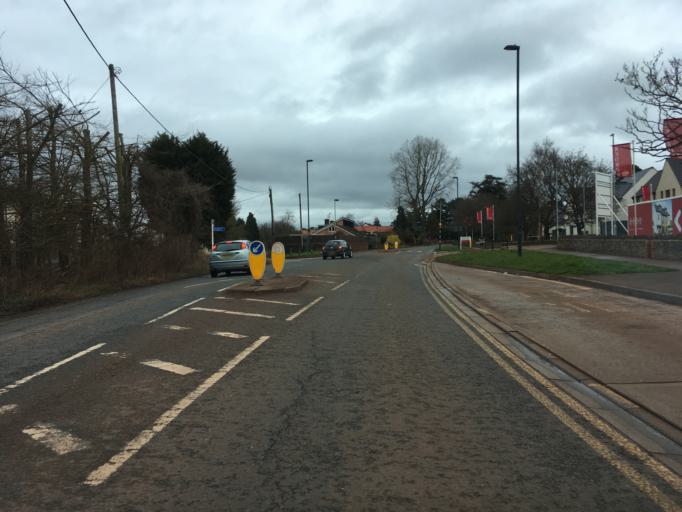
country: GB
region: England
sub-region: South Gloucestershire
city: Stoke Gifford
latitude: 51.4983
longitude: -2.5274
